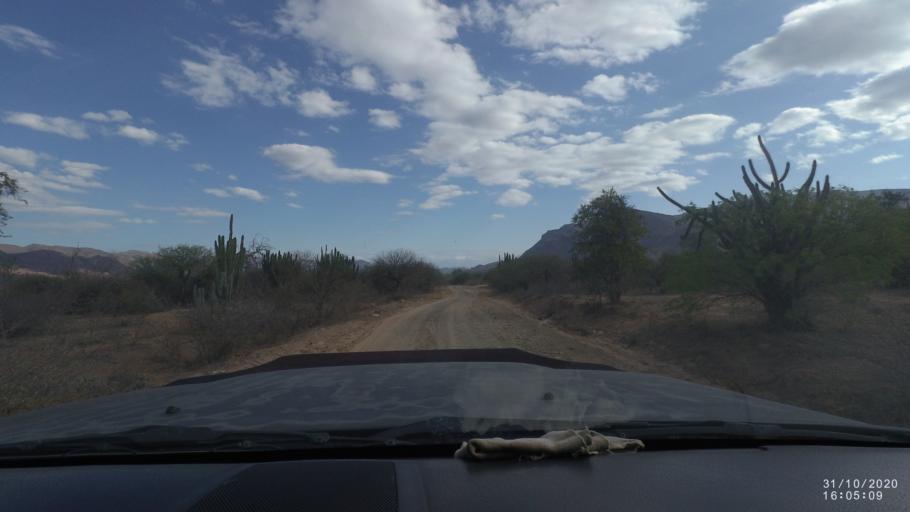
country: BO
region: Chuquisaca
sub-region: Provincia Zudanez
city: Mojocoya
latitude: -18.3644
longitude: -64.6498
